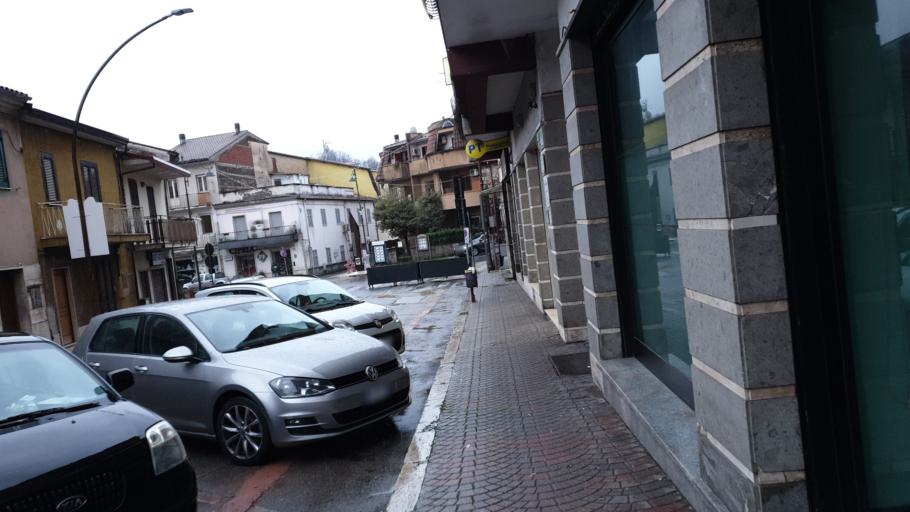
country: IT
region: Latium
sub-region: Provincia di Frosinone
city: Ceccano
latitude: 41.5679
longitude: 13.3306
